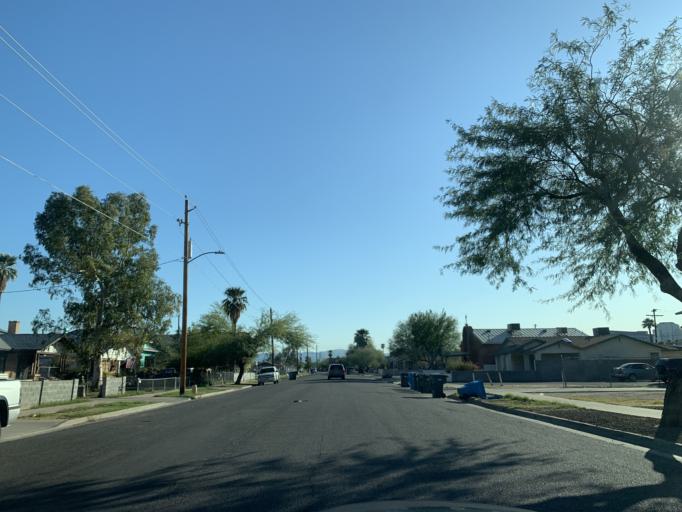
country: US
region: Arizona
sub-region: Maricopa County
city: Phoenix
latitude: 33.4608
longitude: -112.0608
